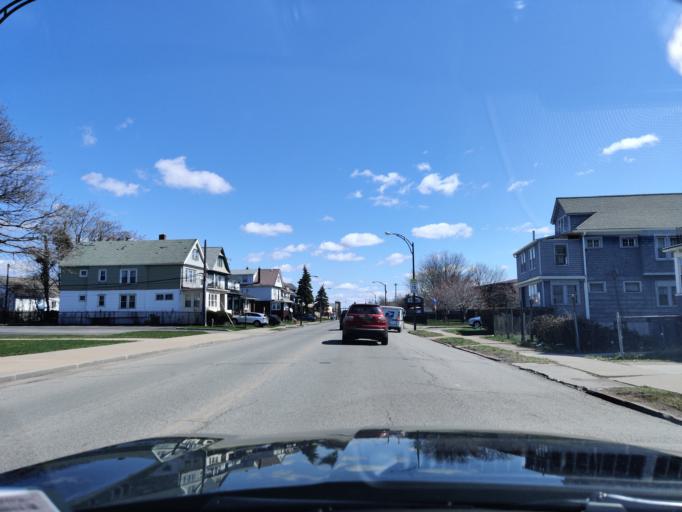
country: US
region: New York
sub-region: Erie County
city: Sloan
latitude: 42.9219
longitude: -78.8324
